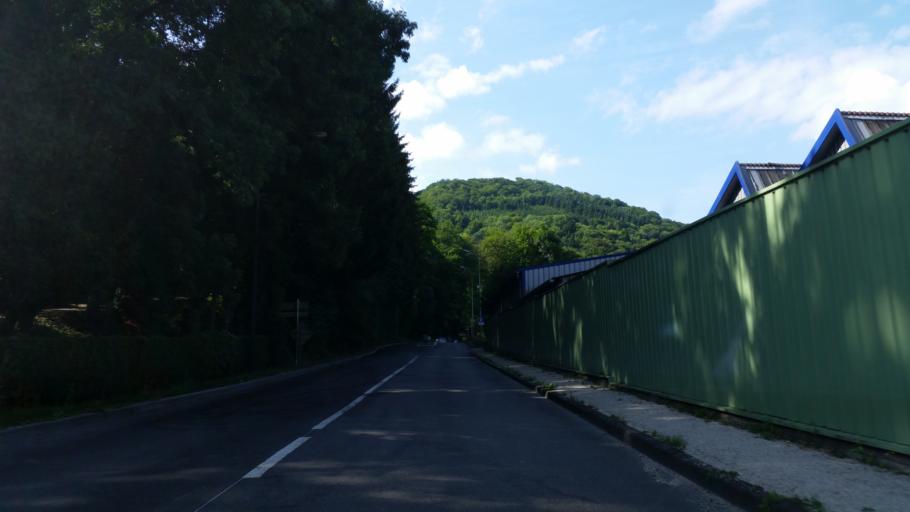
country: FR
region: Franche-Comte
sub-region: Departement du Doubs
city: Pont-de-Roide
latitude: 47.3795
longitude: 6.7728
